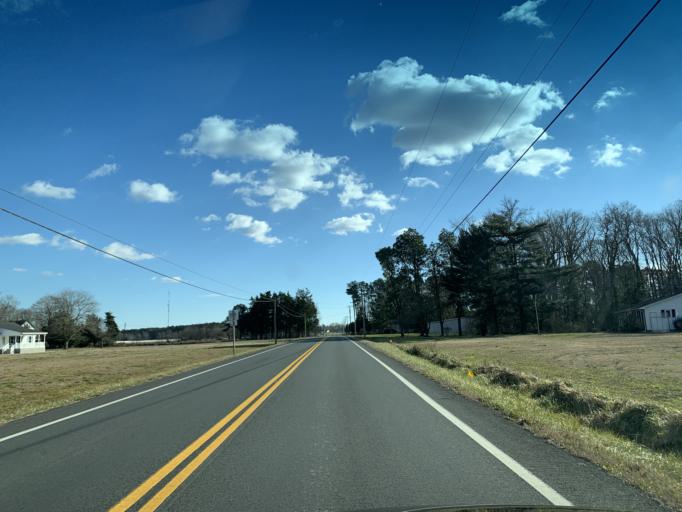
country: US
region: Maryland
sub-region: Worcester County
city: Berlin
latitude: 38.3550
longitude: -75.1961
